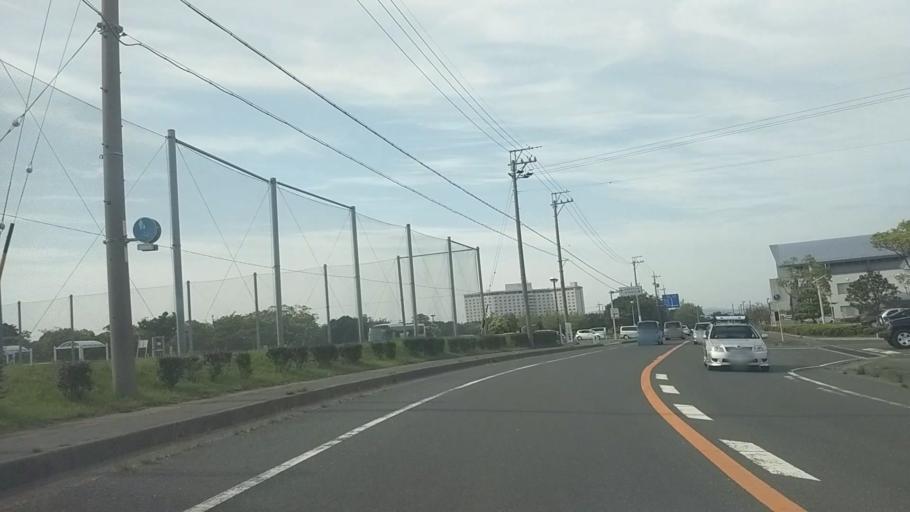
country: JP
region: Shizuoka
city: Kosai-shi
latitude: 34.7011
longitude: 137.6172
